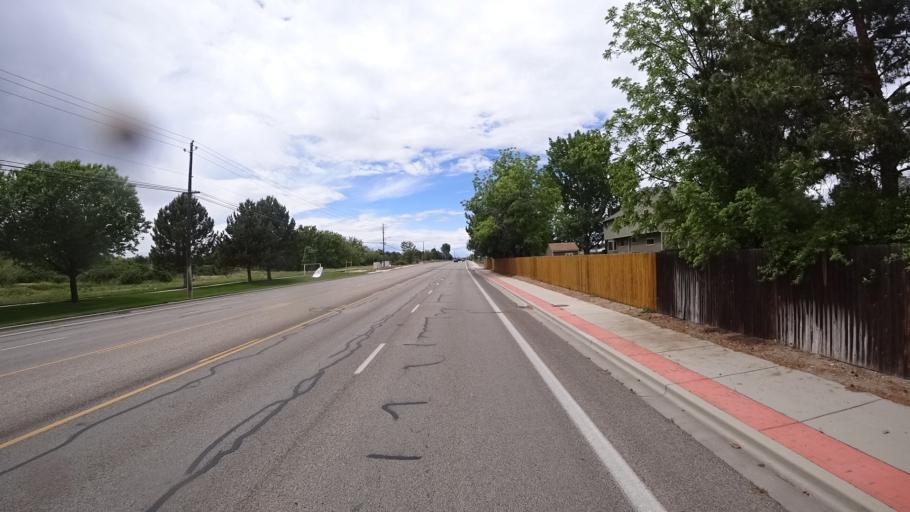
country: US
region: Idaho
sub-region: Ada County
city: Meridian
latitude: 43.5902
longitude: -116.3234
